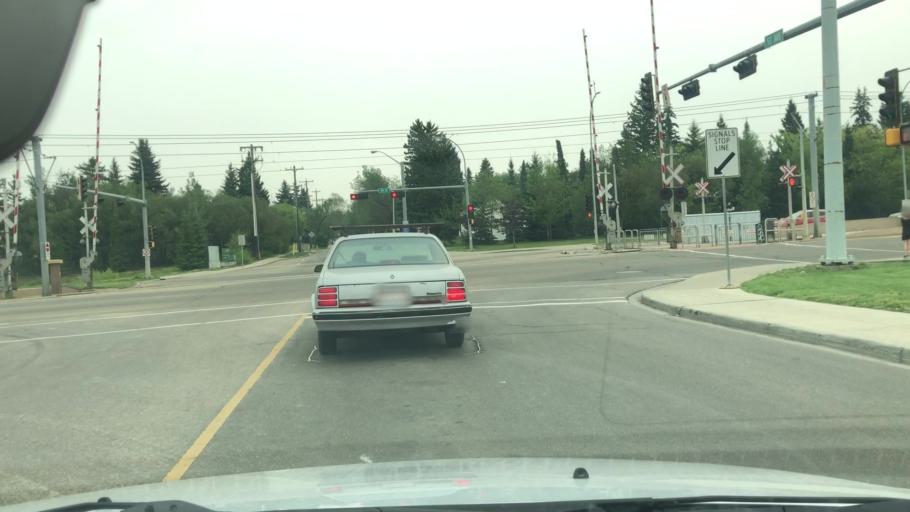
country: CA
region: Alberta
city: Edmonton
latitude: 53.4941
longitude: -113.5174
